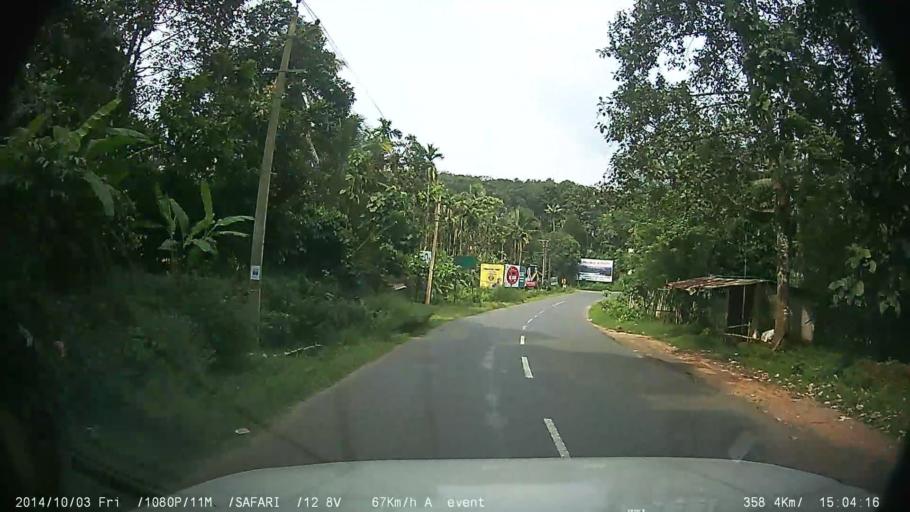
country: IN
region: Kerala
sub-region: Kottayam
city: Palackattumala
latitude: 9.8267
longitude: 76.5887
